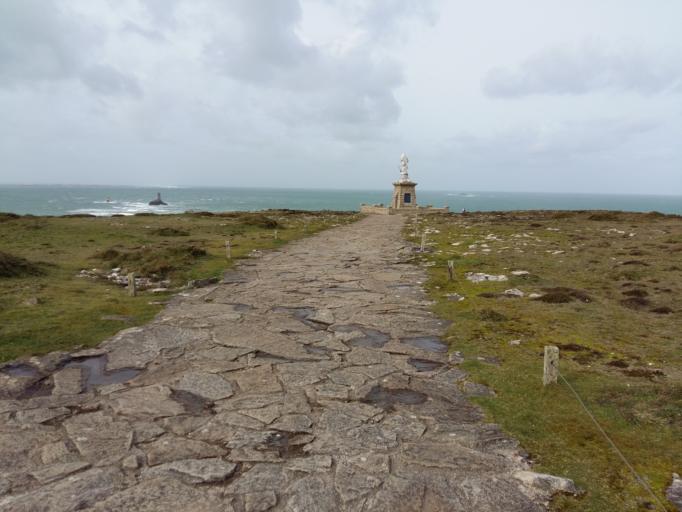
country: FR
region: Brittany
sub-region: Departement du Finistere
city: Plogoff
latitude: 48.0386
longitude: -4.7321
